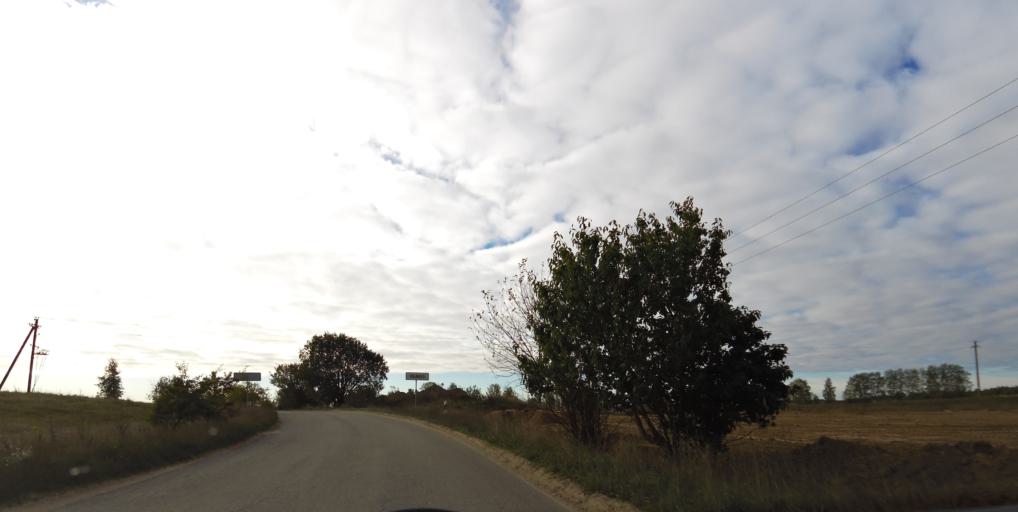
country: LT
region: Vilnius County
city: Pilaite
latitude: 54.7256
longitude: 25.1523
